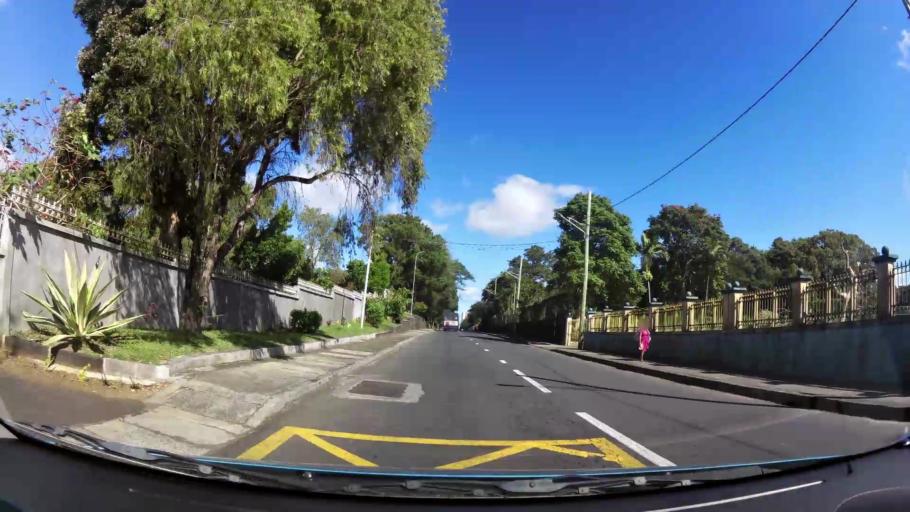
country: MU
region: Plaines Wilhems
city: Vacoas
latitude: -20.2970
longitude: 57.4966
